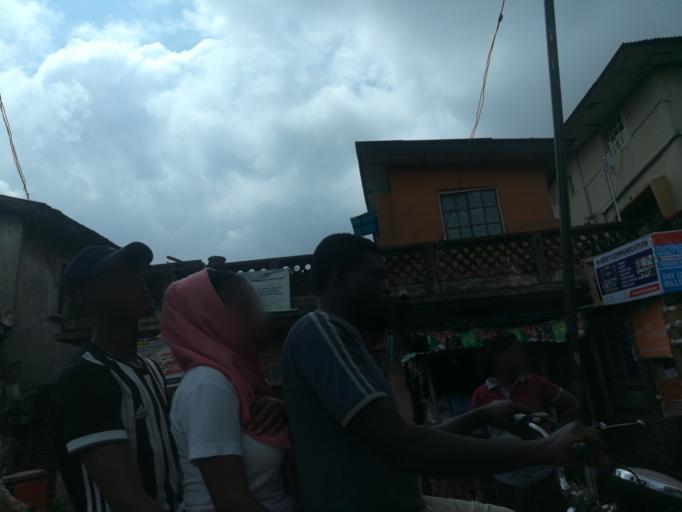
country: NG
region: Lagos
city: Mushin
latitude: 6.5310
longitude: 3.3631
